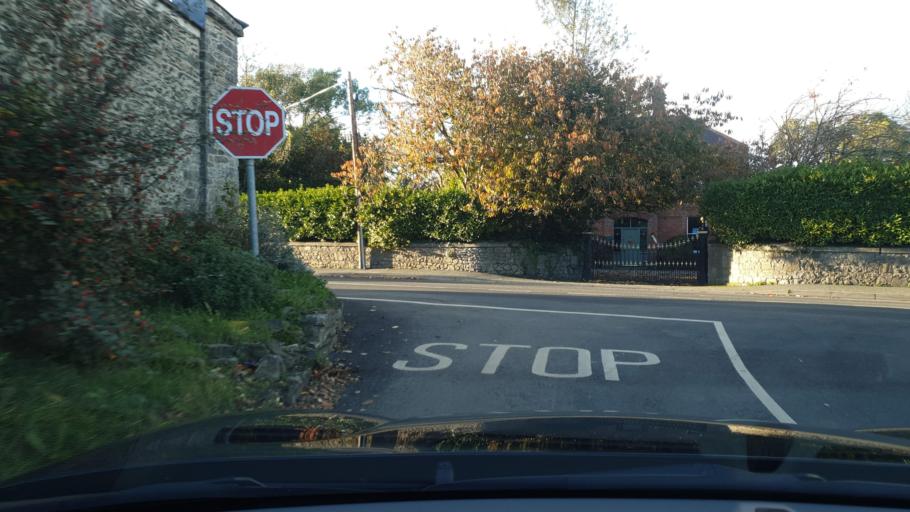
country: IE
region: Leinster
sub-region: An Mhi
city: Stamullin
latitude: 53.6265
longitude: -6.2651
